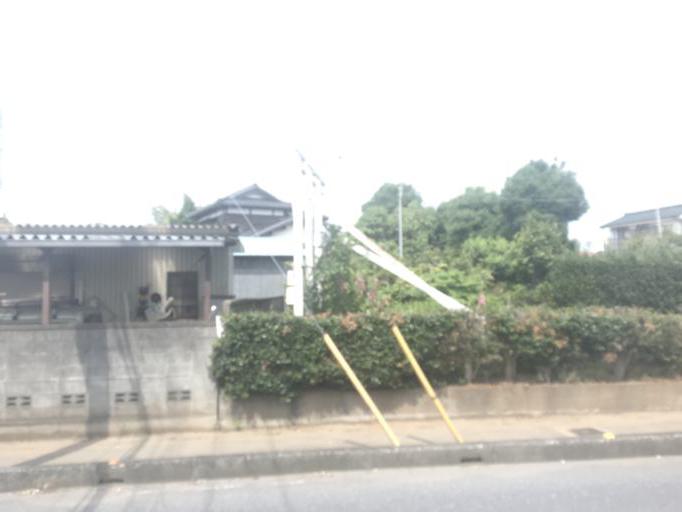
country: JP
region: Saitama
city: Asaka
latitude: 35.7711
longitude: 139.5650
